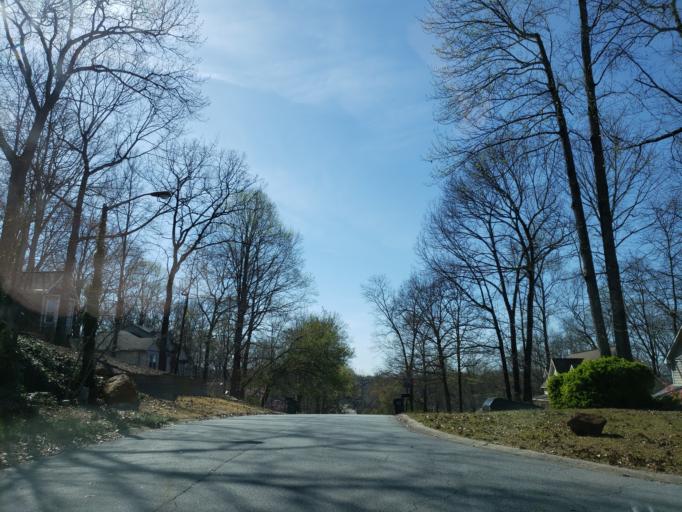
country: US
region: Georgia
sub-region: Cherokee County
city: Woodstock
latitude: 34.0354
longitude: -84.4920
